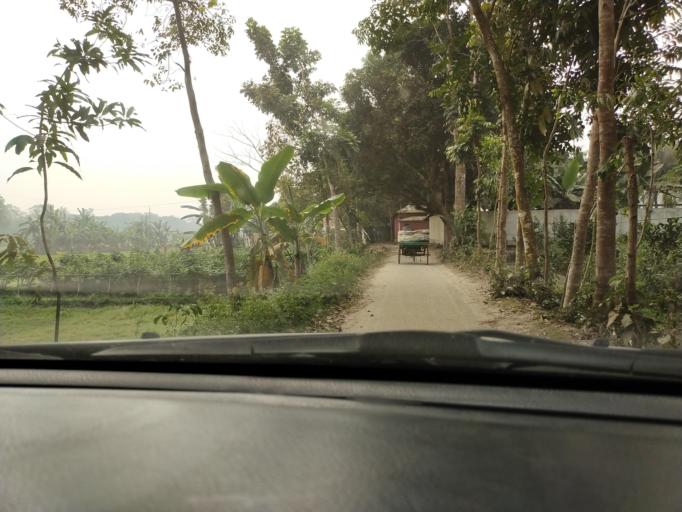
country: BD
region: Dhaka
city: Narsingdi
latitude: 24.0332
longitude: 90.7190
